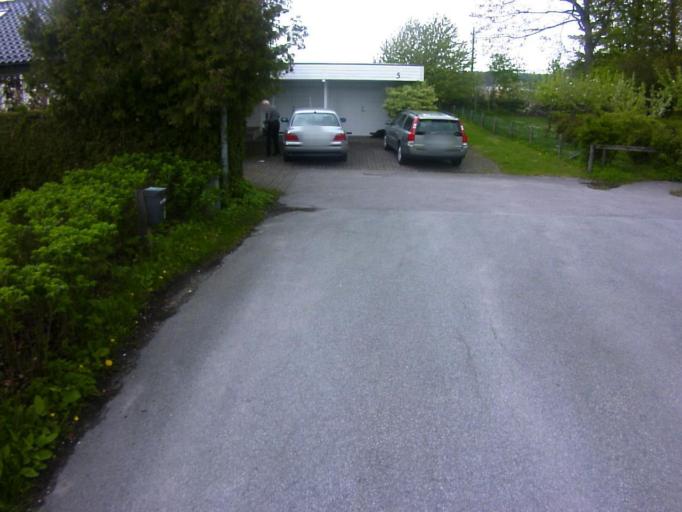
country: SE
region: Blekinge
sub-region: Solvesborgs Kommun
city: Soelvesborg
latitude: 56.0615
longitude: 14.5500
